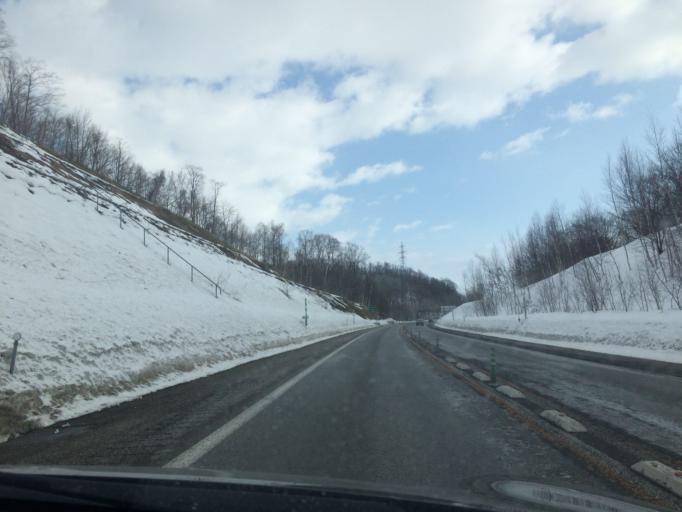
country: JP
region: Hokkaido
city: Chitose
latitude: 42.8852
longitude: 141.7618
